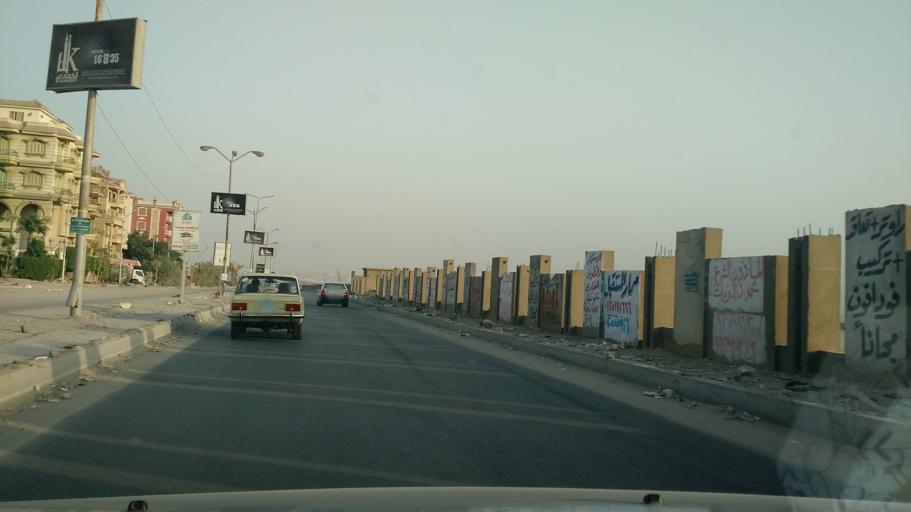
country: EG
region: Muhafazat al Qahirah
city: Cairo
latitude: 29.9997
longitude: 31.2891
